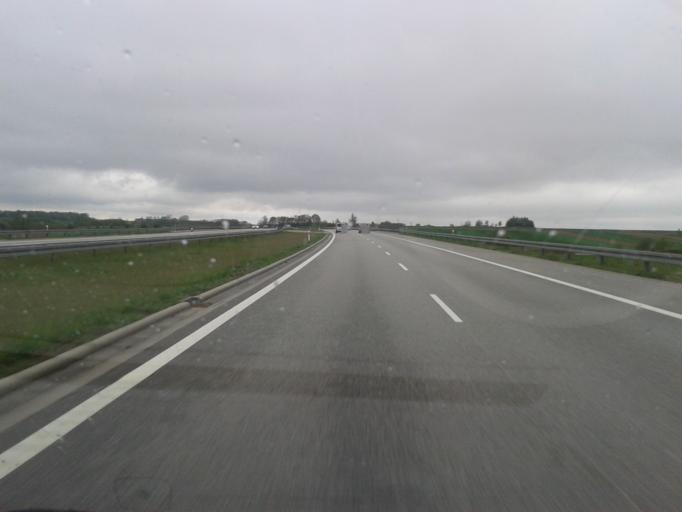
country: PL
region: Subcarpathian Voivodeship
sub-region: Powiat debicki
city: Czarna
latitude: 50.0980
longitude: 21.2865
